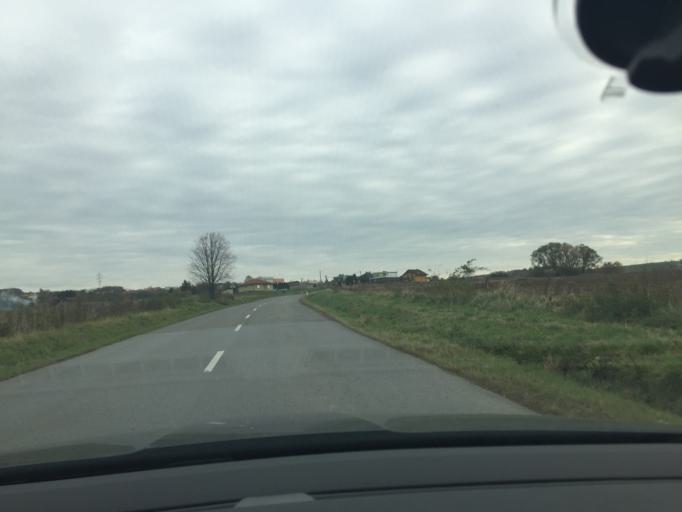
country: SK
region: Presovsky
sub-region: Okres Presov
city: Presov
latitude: 48.9502
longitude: 21.2839
